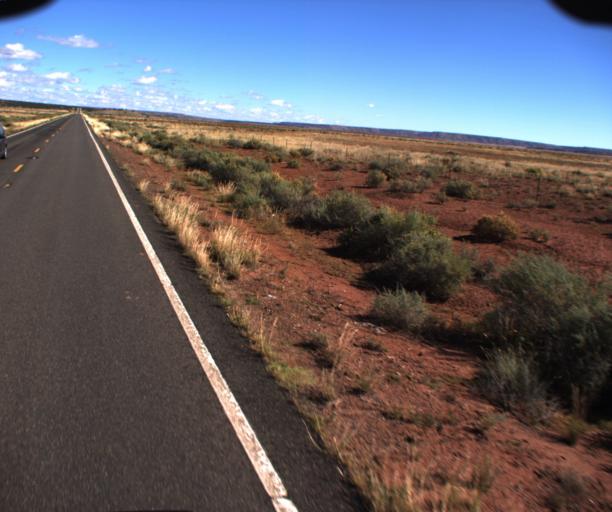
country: US
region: Arizona
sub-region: Apache County
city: Saint Johns
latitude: 34.7041
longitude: -109.2691
